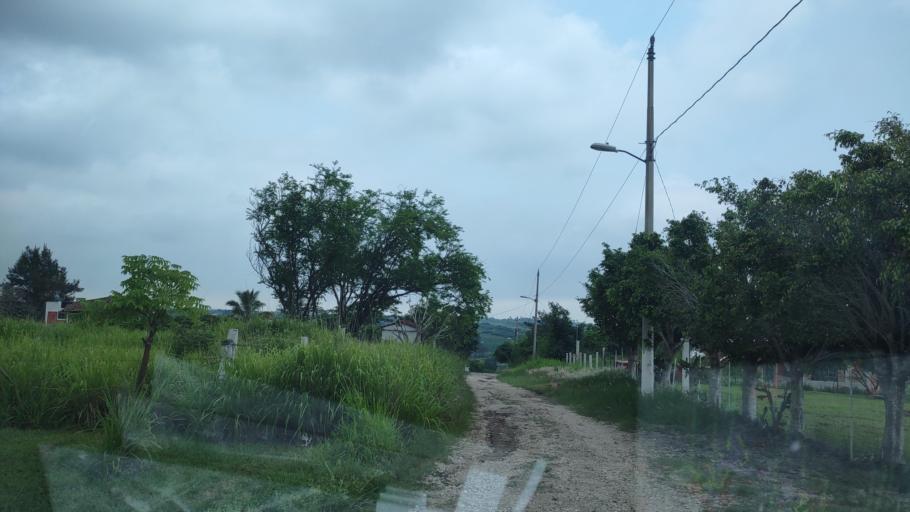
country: MX
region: Veracruz
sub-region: Emiliano Zapata
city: Dos Rios
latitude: 19.4774
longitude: -96.8157
